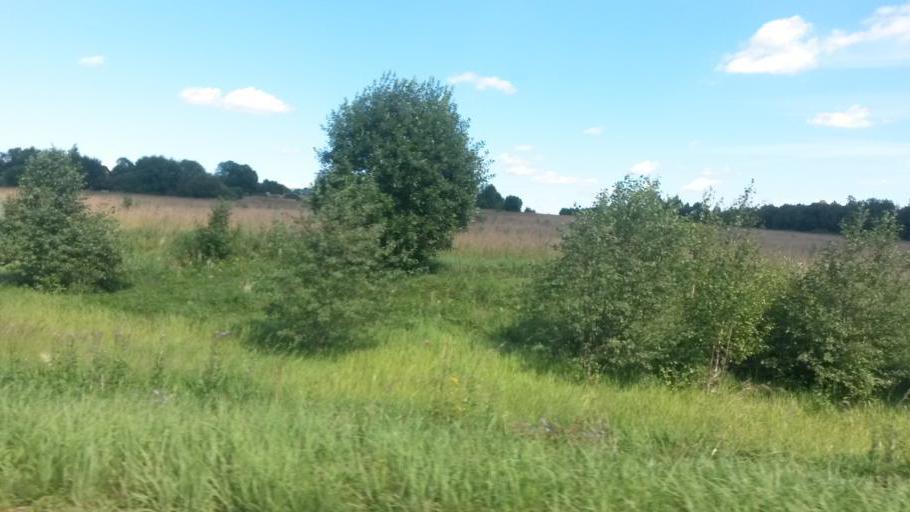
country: RU
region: Jaroslavl
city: Gavrilov-Yam
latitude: 57.4434
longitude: 39.9162
